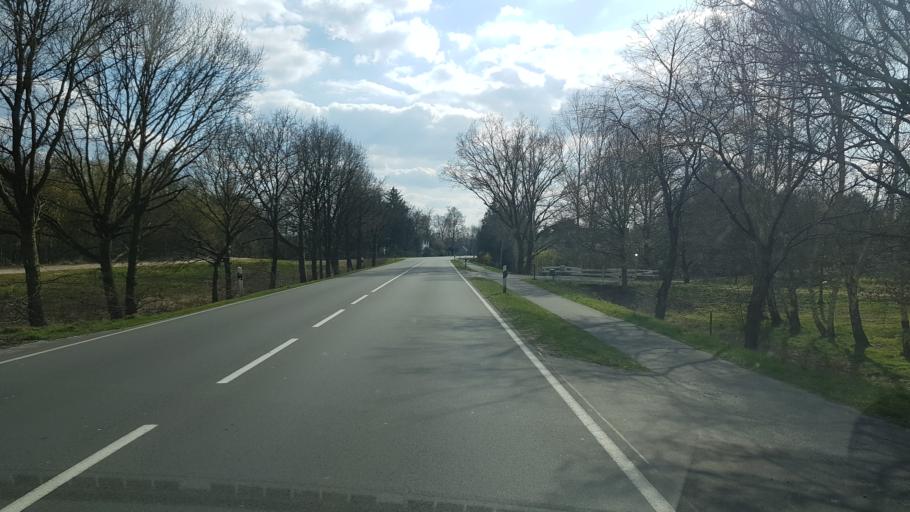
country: DE
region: Lower Saxony
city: Rastede
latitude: 53.2493
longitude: 8.2977
